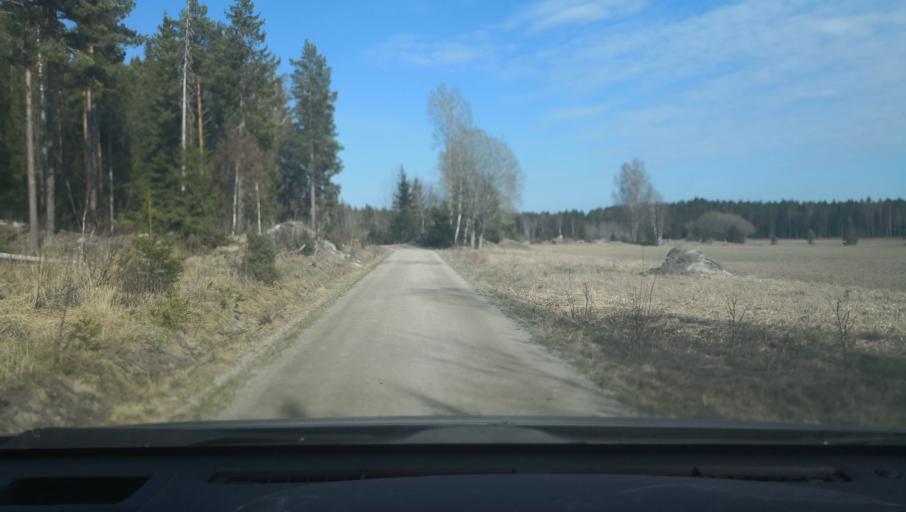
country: SE
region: Uppsala
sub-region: Heby Kommun
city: Heby
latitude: 59.8390
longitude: 16.8762
